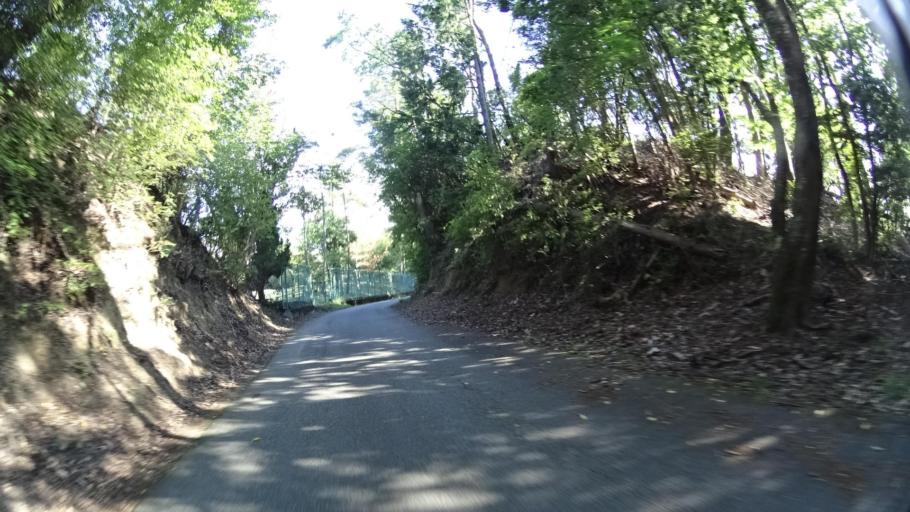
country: JP
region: Kyoto
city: Kameoka
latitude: 34.9811
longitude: 135.5568
